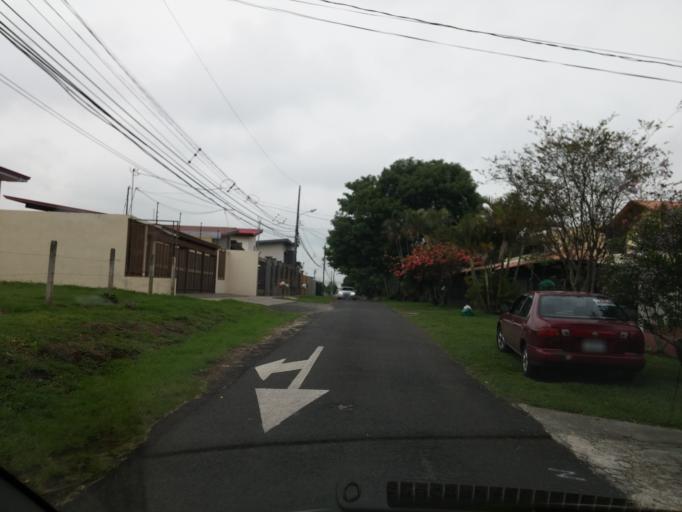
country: CR
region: Heredia
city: Mercedes
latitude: 10.0169
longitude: -84.1487
